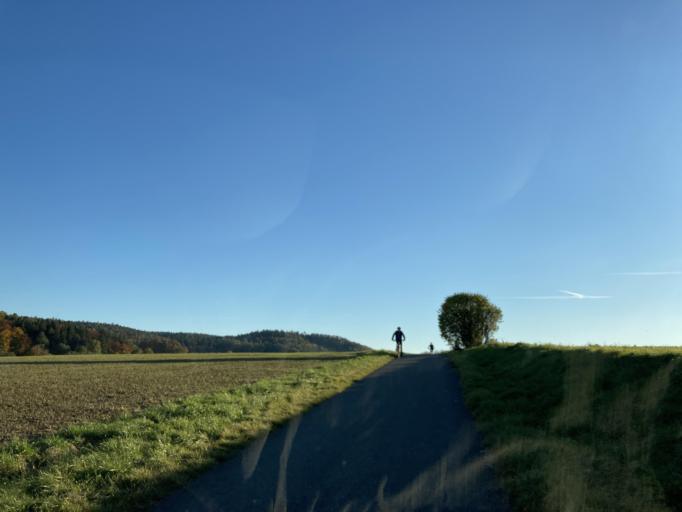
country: DE
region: Baden-Wuerttemberg
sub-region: Tuebingen Region
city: Rottenburg
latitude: 48.4317
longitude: 8.9314
